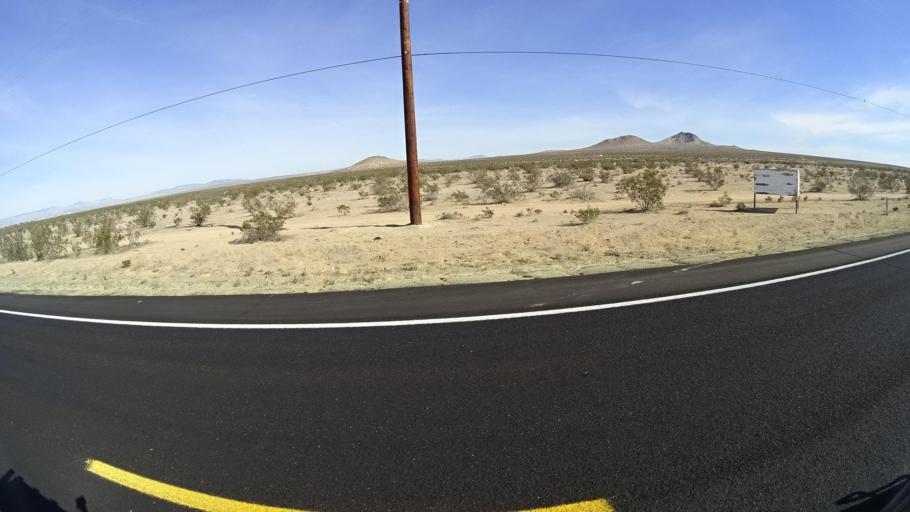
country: US
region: California
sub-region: Kern County
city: California City
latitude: 35.1047
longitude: -117.9211
